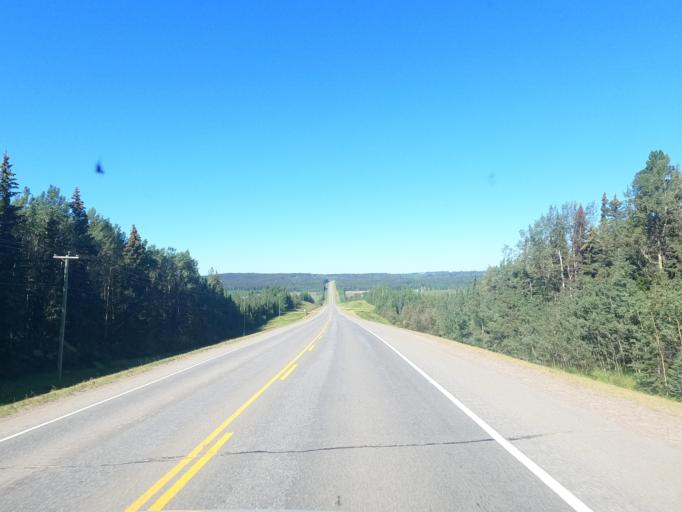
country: CA
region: British Columbia
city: Fort St. John
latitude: 56.6300
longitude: -121.5214
